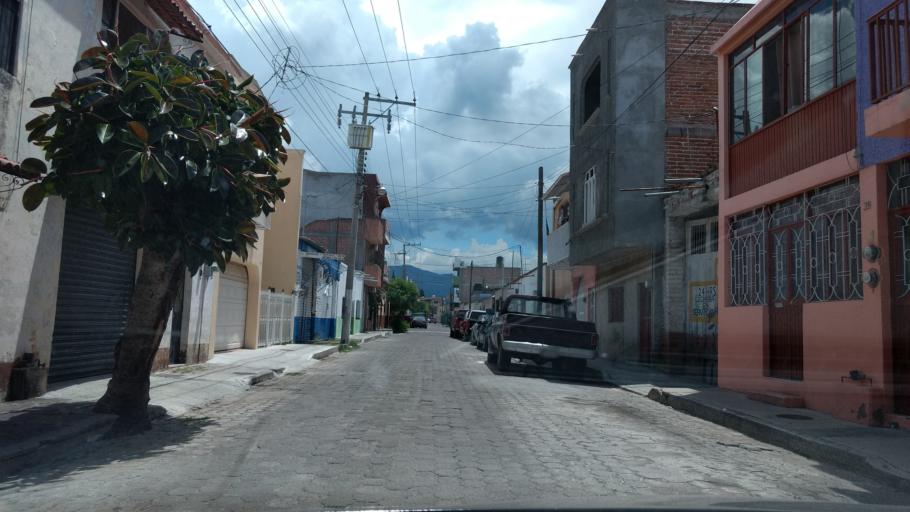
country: MX
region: Zacatecas
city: Tlaltenango de Sanchez Roman
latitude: 21.7837
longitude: -103.3023
